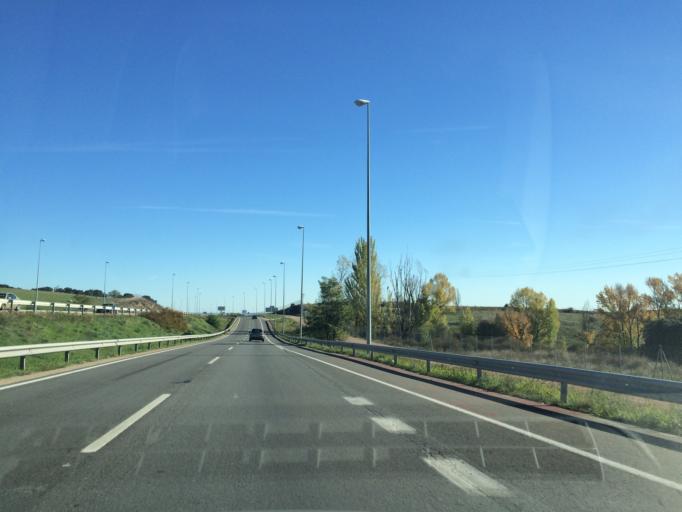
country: ES
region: Madrid
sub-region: Provincia de Madrid
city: Colmenar Viejo
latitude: 40.6554
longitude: -3.7449
